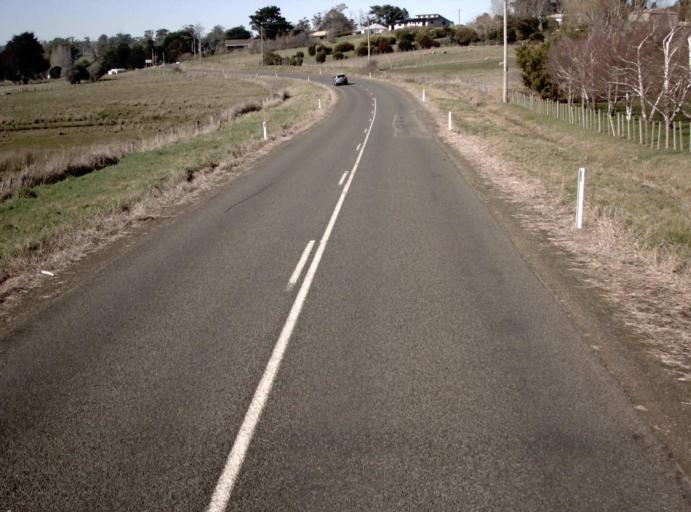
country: AU
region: Tasmania
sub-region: Launceston
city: Mayfield
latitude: -41.3271
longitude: 147.0667
